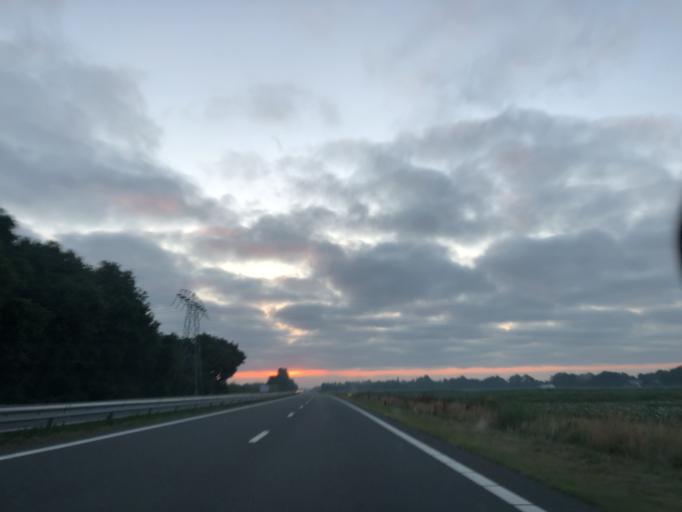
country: NL
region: Drenthe
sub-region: Gemeente Aa en Hunze
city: Anloo
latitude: 53.0232
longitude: 6.7797
